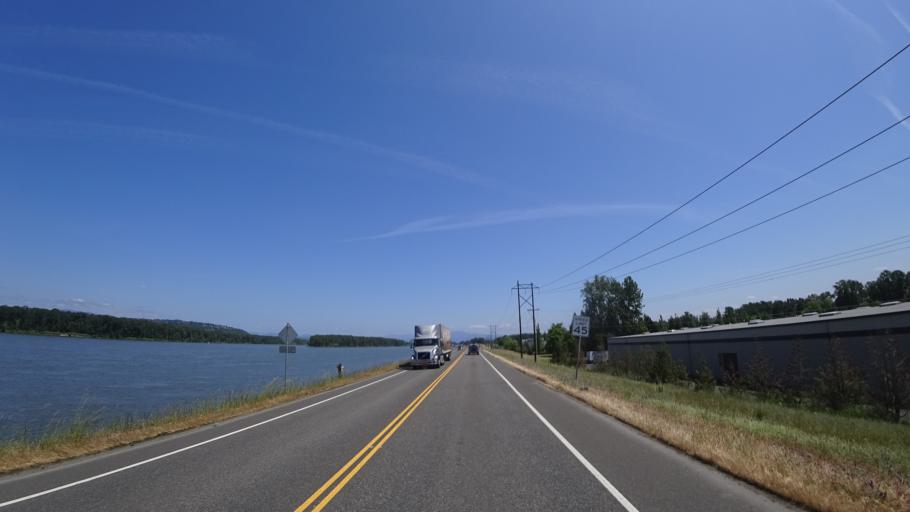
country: US
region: Oregon
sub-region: Multnomah County
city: Fairview
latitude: 45.5611
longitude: -122.4974
